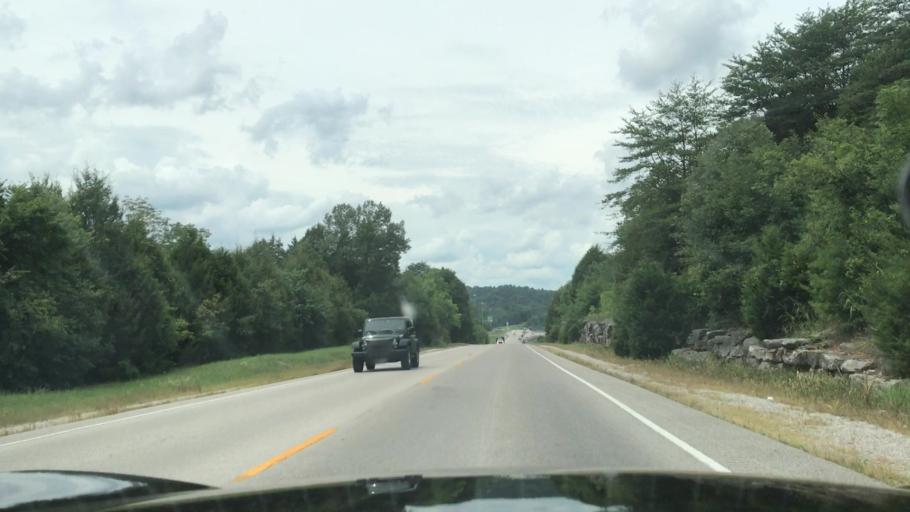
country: US
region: Kentucky
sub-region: Hart County
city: Horse Cave
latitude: 37.1965
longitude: -85.9292
